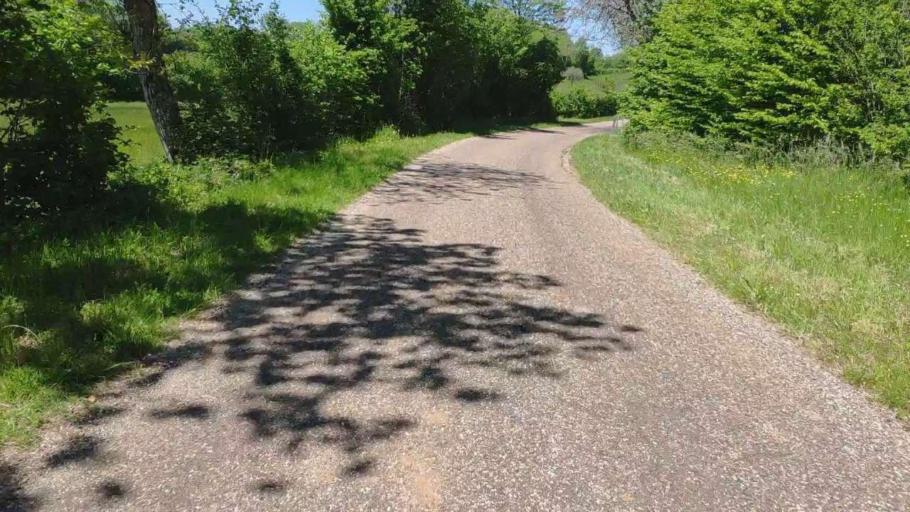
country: FR
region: Franche-Comte
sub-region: Departement du Jura
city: Poligny
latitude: 46.7395
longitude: 5.6753
